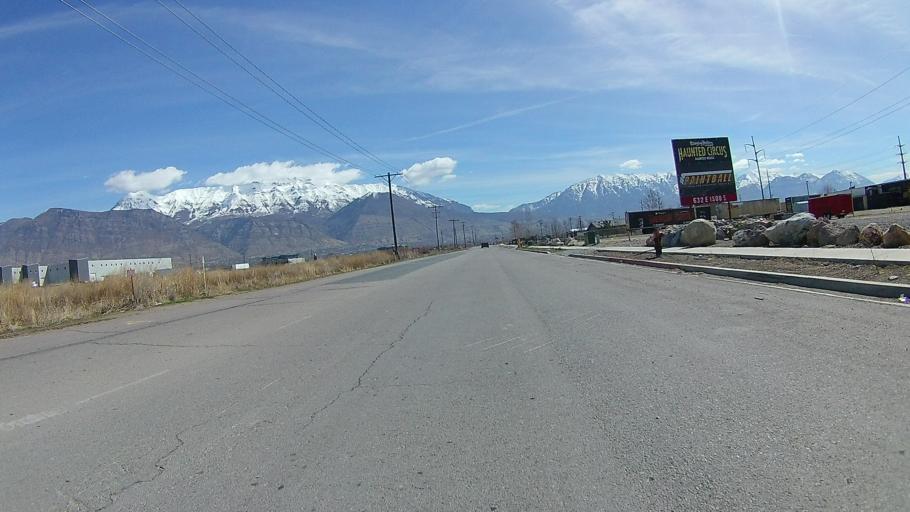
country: US
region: Utah
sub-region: Utah County
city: American Fork
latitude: 40.3476
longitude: -111.7828
